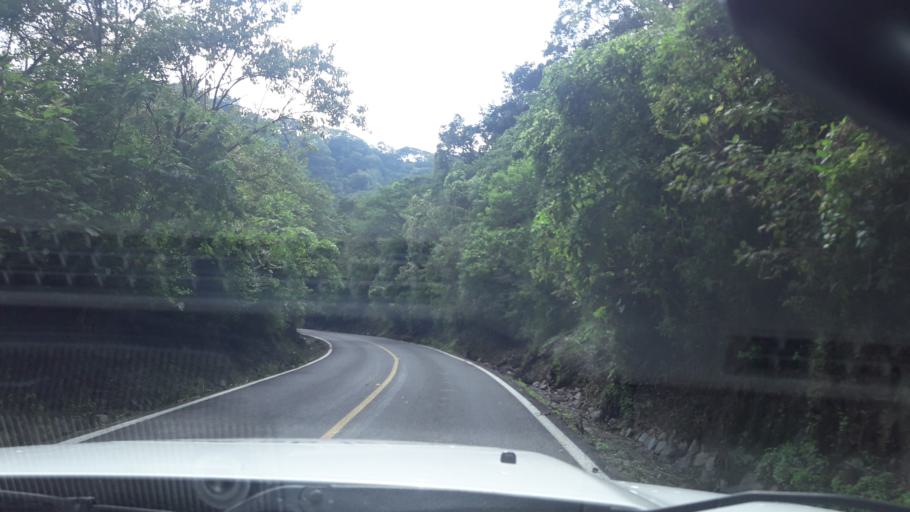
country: MX
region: Colima
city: Suchitlan
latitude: 19.4423
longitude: -103.7151
